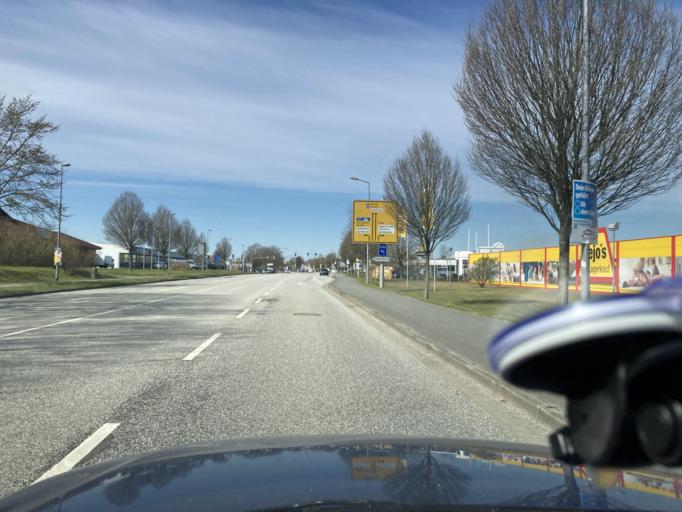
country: DE
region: Schleswig-Holstein
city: Heide
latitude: 54.1977
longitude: 9.1278
